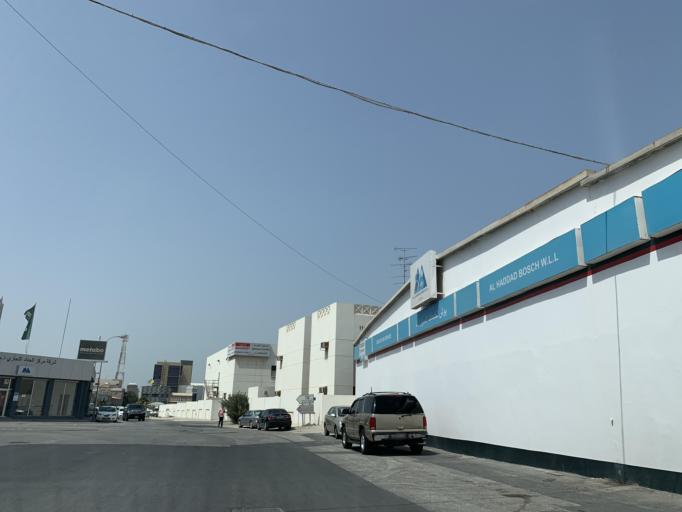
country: BH
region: Northern
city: Madinat `Isa
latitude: 26.1882
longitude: 50.5380
